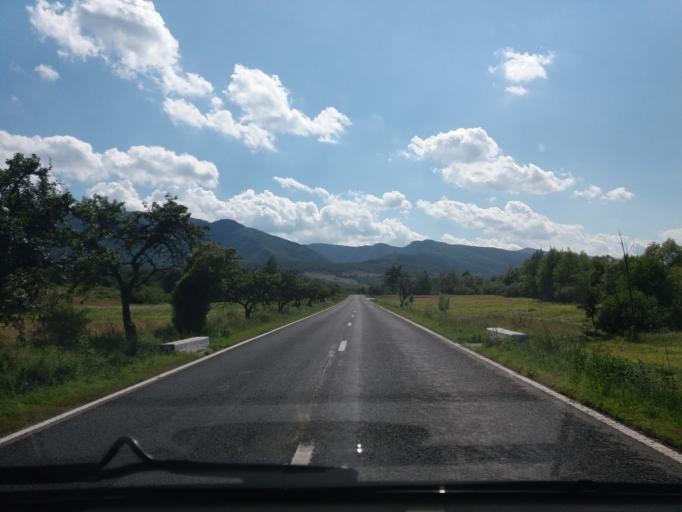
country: RO
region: Hunedoara
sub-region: Comuna Sarmizegetusa
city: Sarmizegetusa
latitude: 45.5119
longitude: 22.7393
